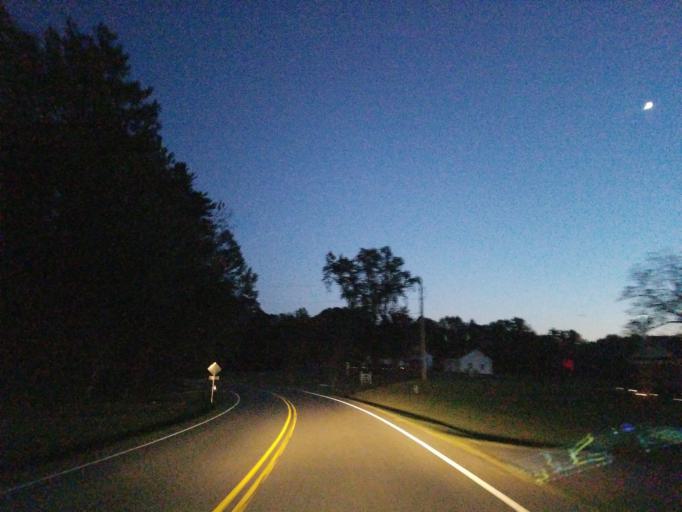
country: US
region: Georgia
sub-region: Dawson County
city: Dawsonville
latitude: 34.4318
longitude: -84.1029
